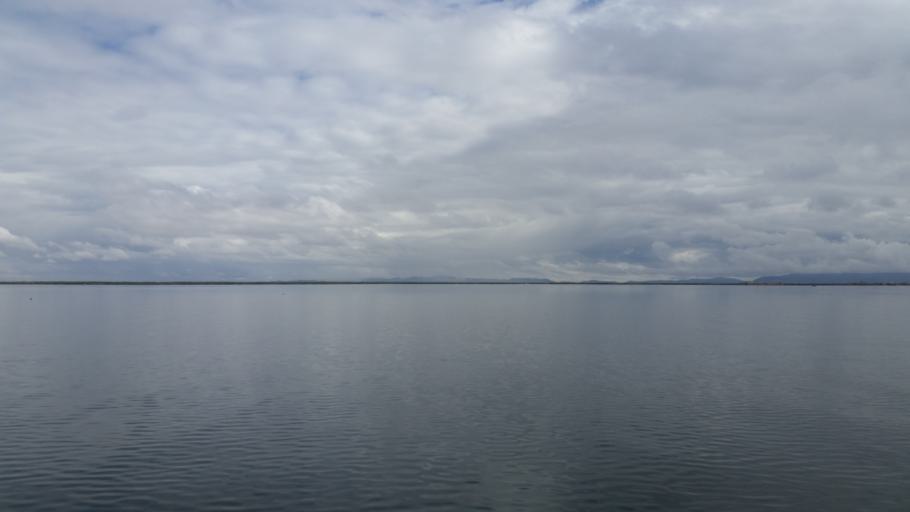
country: PE
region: Puno
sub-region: Provincia de Puno
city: Puno
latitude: -15.8480
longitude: -69.9559
